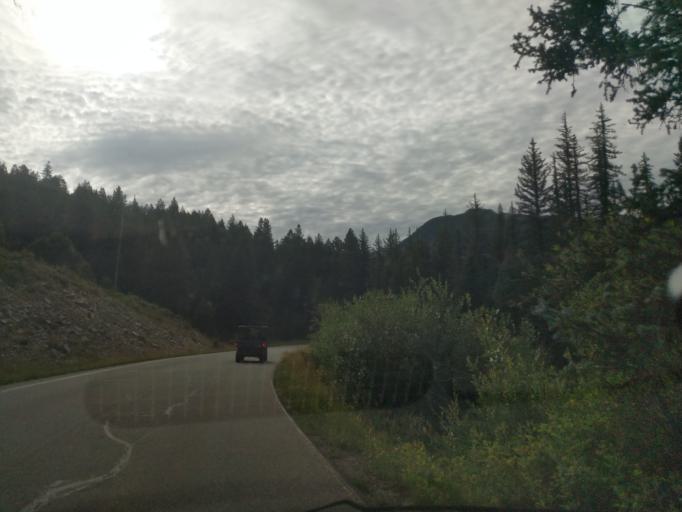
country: US
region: Colorado
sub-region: Gunnison County
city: Crested Butte
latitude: 39.0784
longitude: -107.2264
